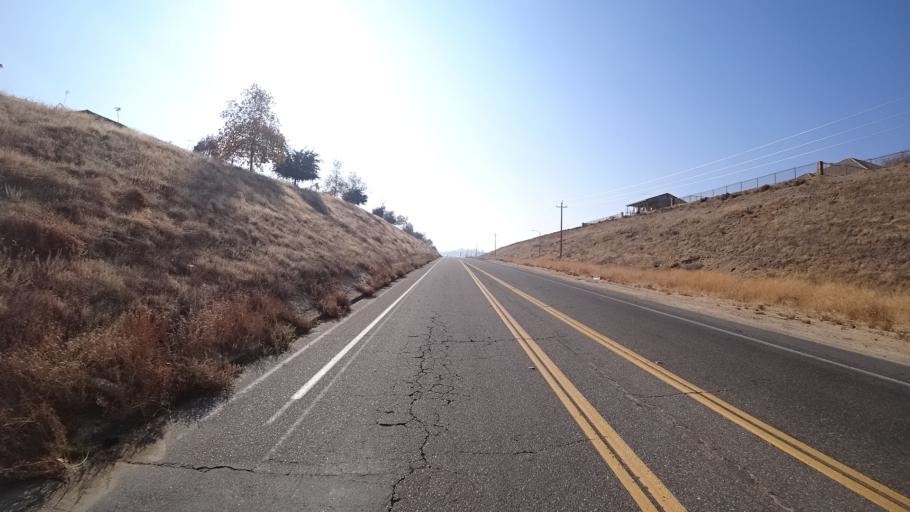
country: US
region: California
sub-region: Kern County
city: Oildale
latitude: 35.4161
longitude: -118.8589
